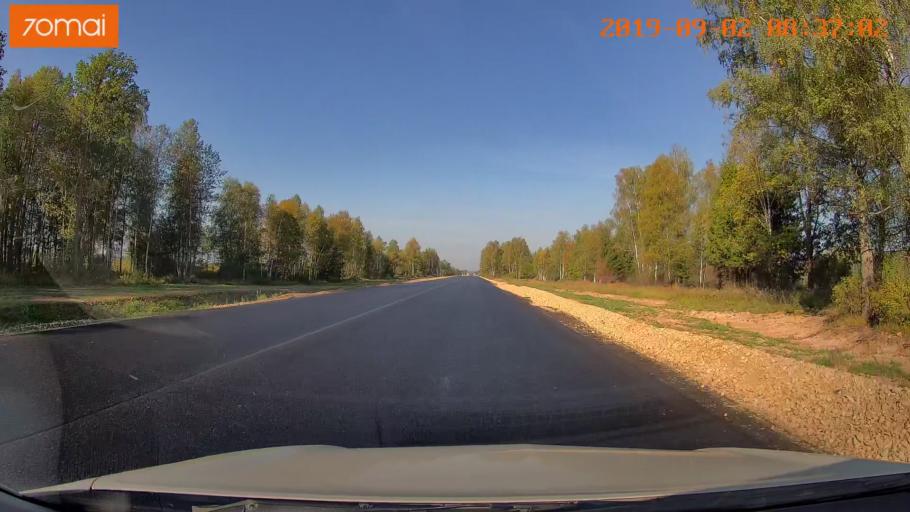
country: RU
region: Kaluga
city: Kudinovo
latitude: 54.9806
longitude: 36.2072
